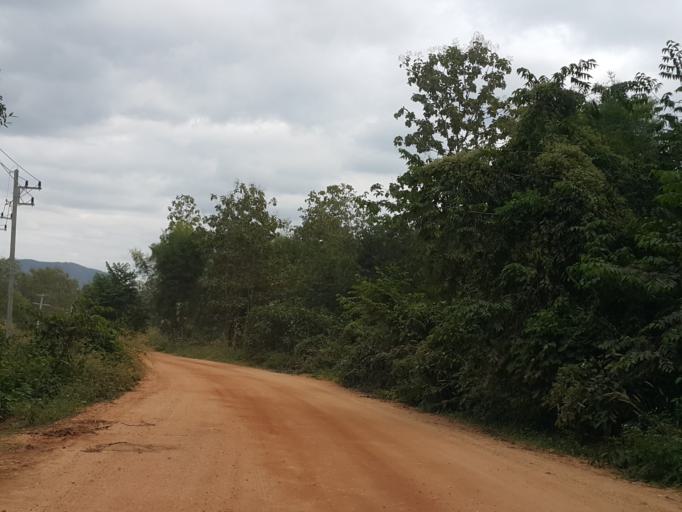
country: TH
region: Lampang
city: Chae Hom
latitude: 18.5780
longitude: 99.4536
